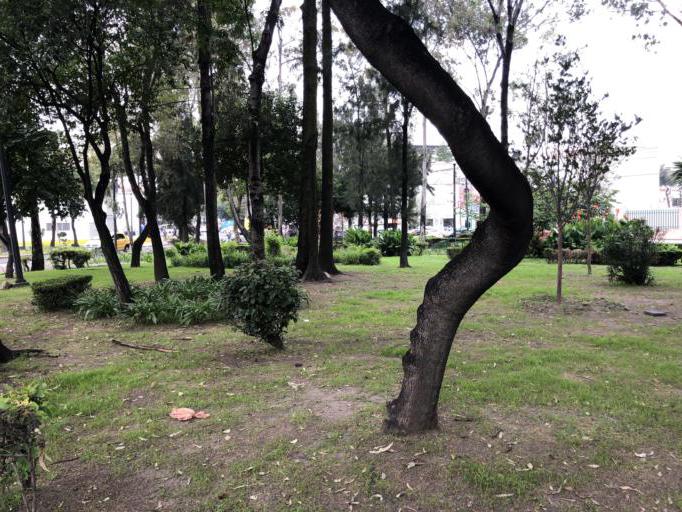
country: MX
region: Mexico City
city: Cuauhtemoc
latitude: 19.4534
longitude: -99.1312
